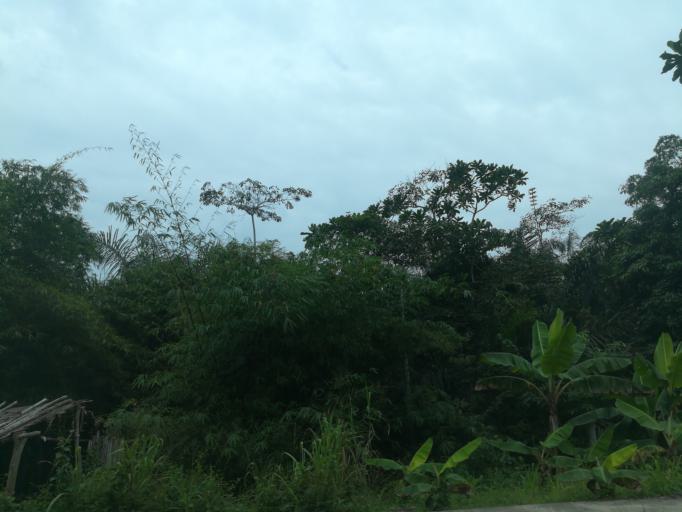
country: NG
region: Lagos
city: Ejirin
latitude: 6.6511
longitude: 3.7901
